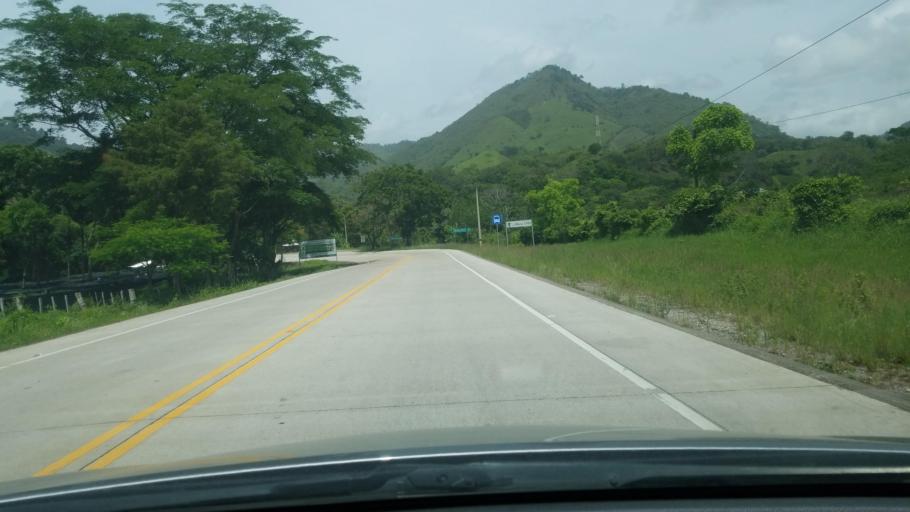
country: HN
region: Copan
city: Veracruz
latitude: 14.8863
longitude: -88.7695
